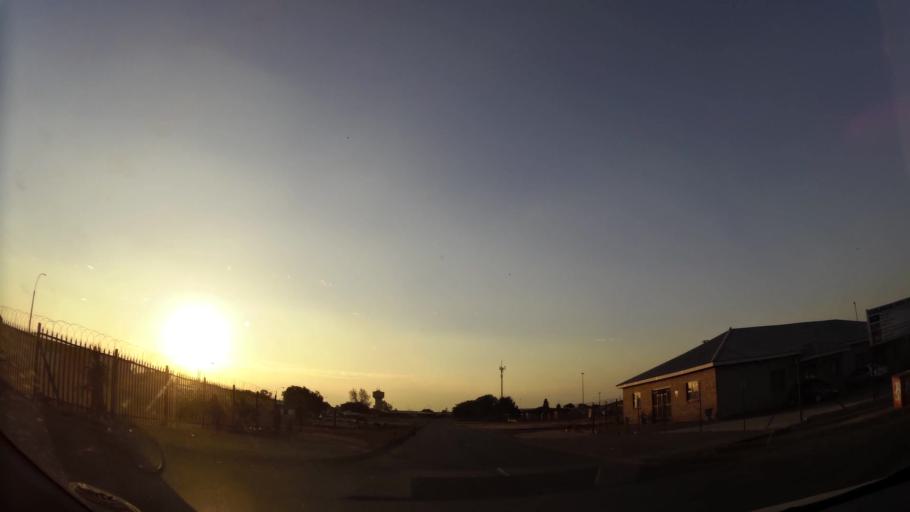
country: ZA
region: Gauteng
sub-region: West Rand District Municipality
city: Randfontein
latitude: -26.2063
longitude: 27.7044
